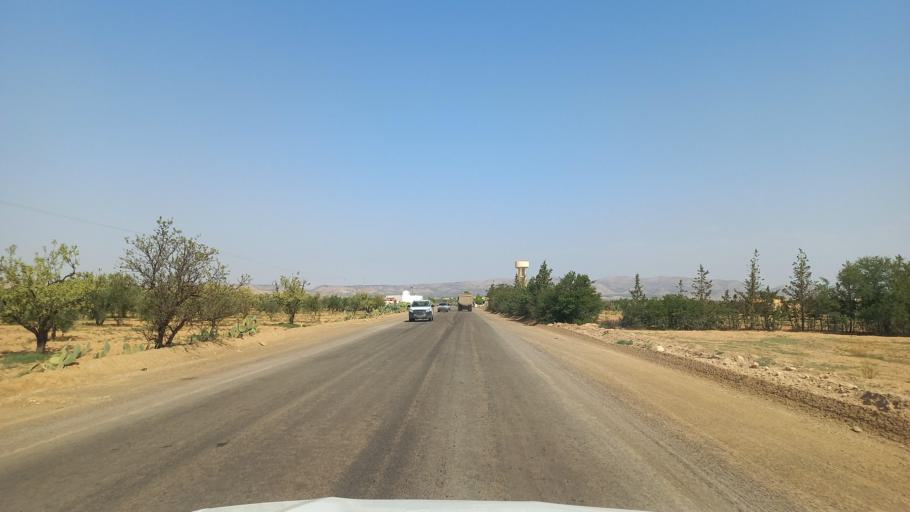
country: TN
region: Al Qasrayn
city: Sbiba
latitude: 35.3519
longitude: 9.0511
